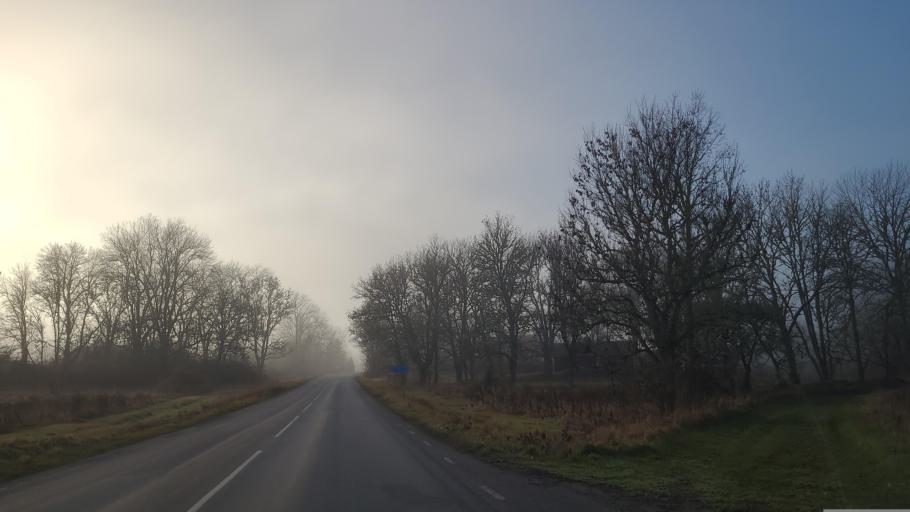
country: SE
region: Uppsala
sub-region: Enkopings Kommun
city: Grillby
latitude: 59.5951
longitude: 17.2286
